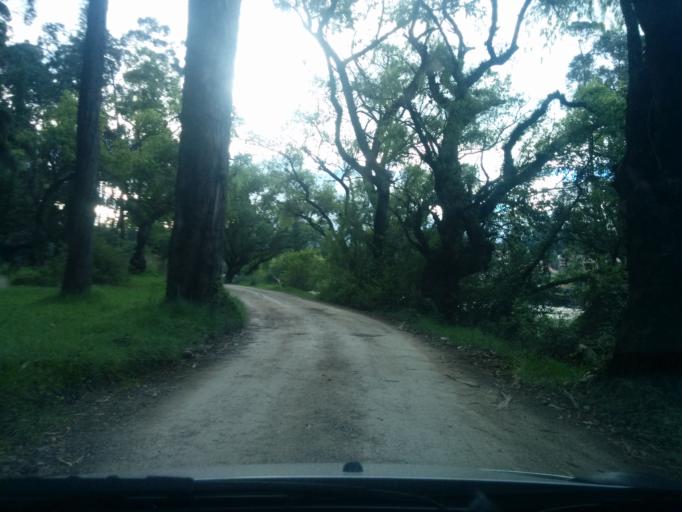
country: EC
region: Azuay
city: Cuenca
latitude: -2.8842
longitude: -78.9491
